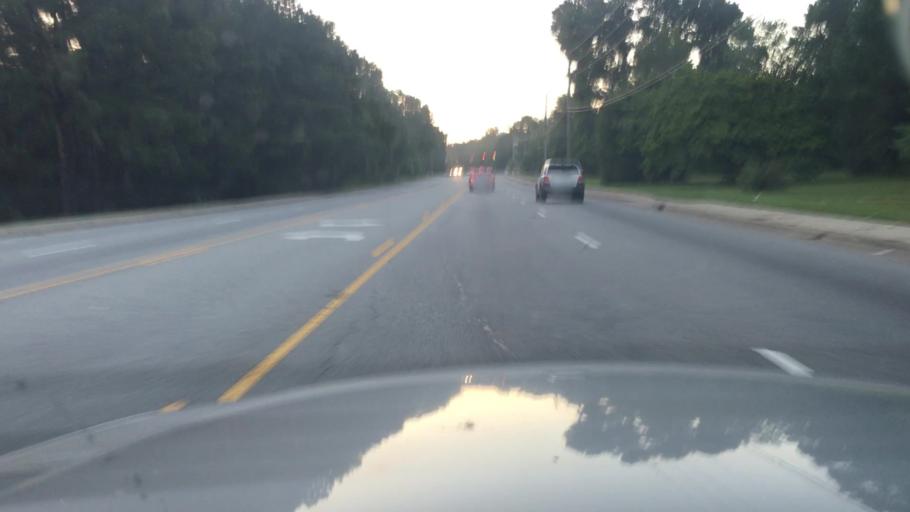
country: US
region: North Carolina
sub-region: Cumberland County
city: Fort Bragg
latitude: 35.0589
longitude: -79.0063
